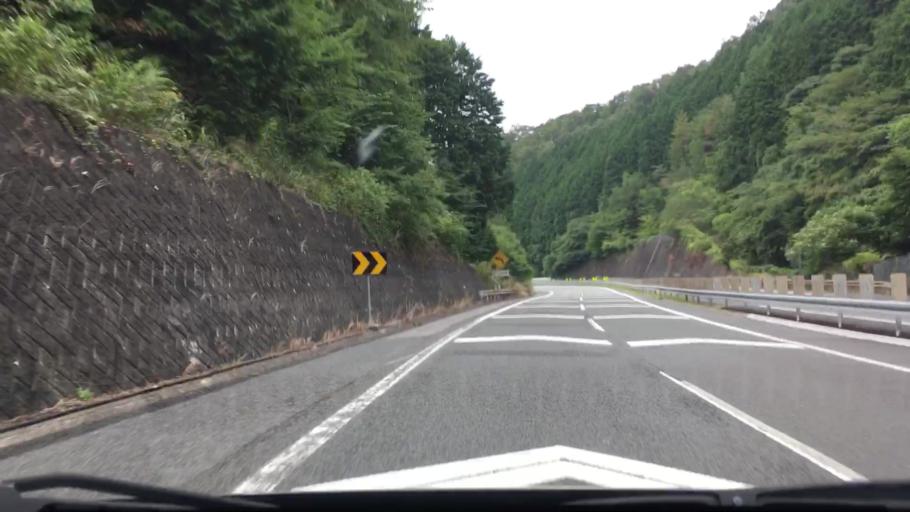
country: JP
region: Hiroshima
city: Shobara
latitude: 34.8899
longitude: 133.1983
